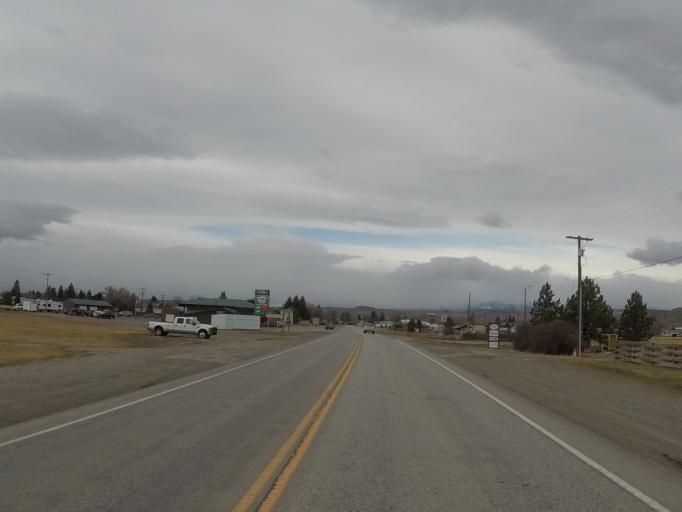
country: US
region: Montana
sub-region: Sweet Grass County
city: Big Timber
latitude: 45.8361
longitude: -109.9403
